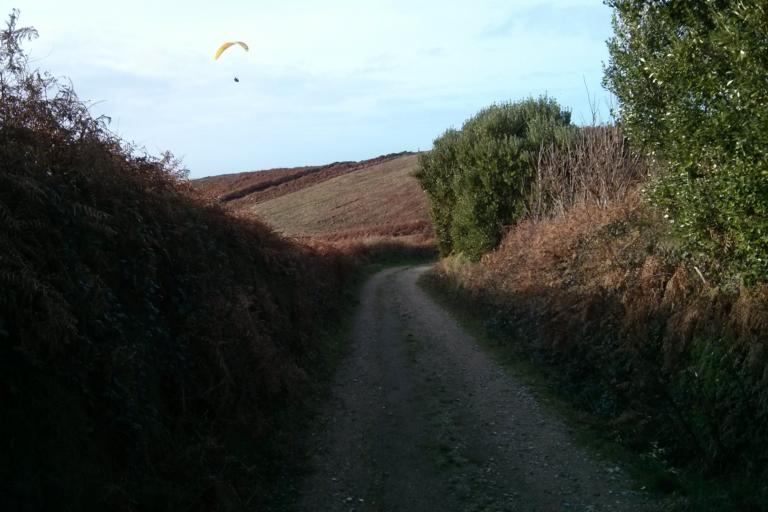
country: FR
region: Brittany
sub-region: Departement du Finistere
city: Le Conquet
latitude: 48.3986
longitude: -4.7719
